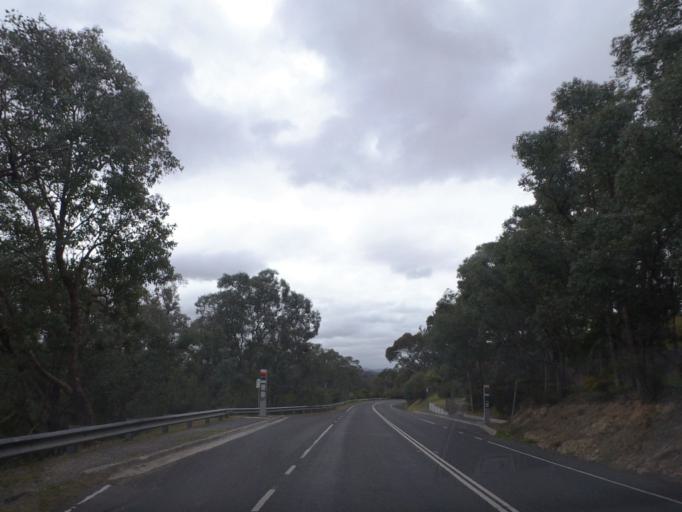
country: AU
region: Victoria
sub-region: Nillumbik
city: North Warrandyte
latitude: -37.7458
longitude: 145.2007
